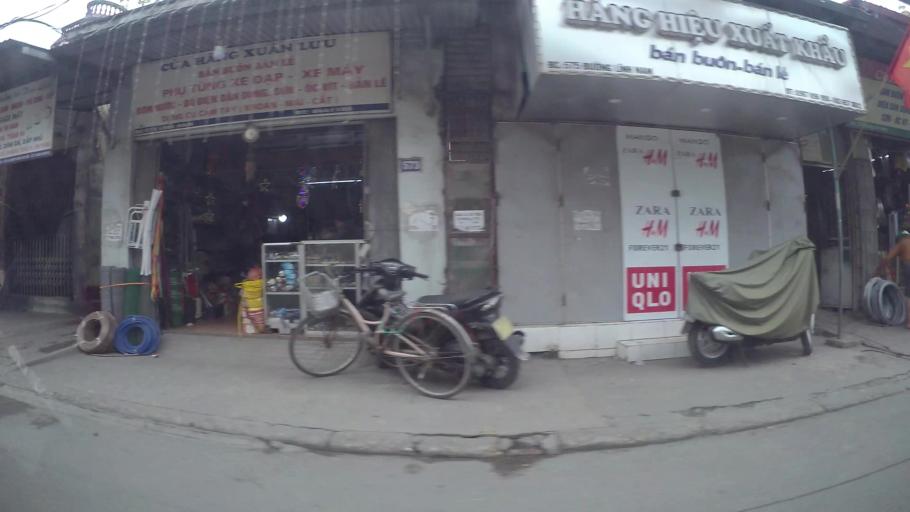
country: VN
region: Ha Noi
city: Hai BaTrung
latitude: 20.9802
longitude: 105.8857
